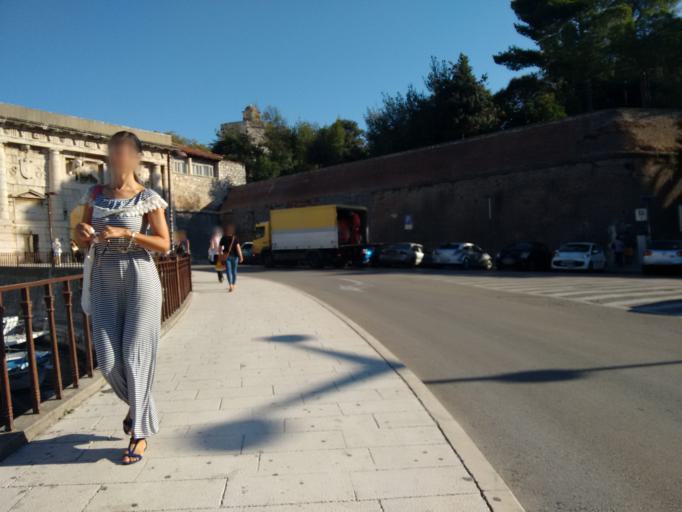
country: HR
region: Zadarska
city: Zadar
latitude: 44.1117
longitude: 15.2286
